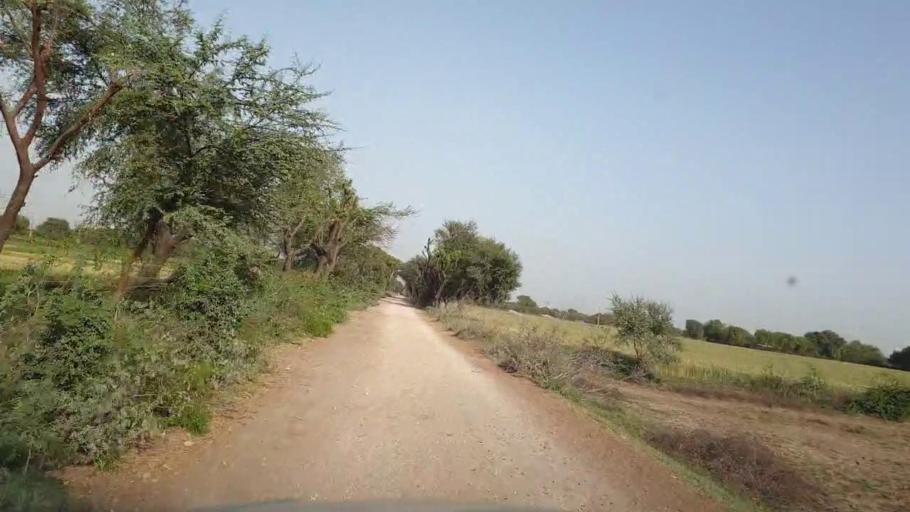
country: PK
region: Sindh
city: Tando Ghulam Ali
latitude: 25.0819
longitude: 68.8849
